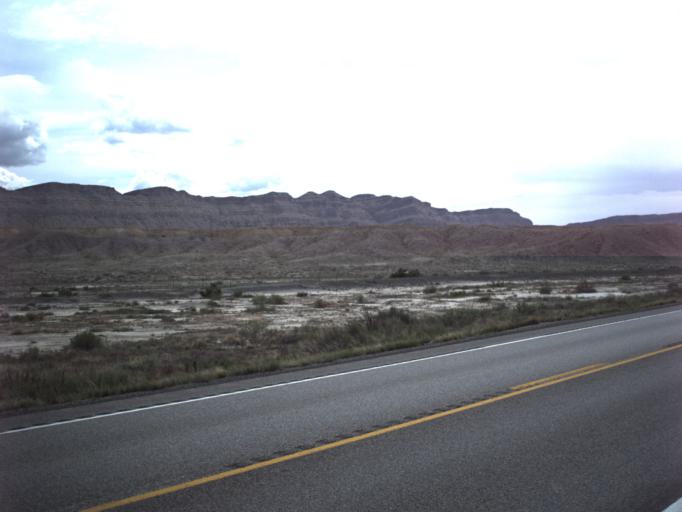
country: US
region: Utah
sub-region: Carbon County
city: East Carbon City
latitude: 39.3166
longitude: -110.3633
